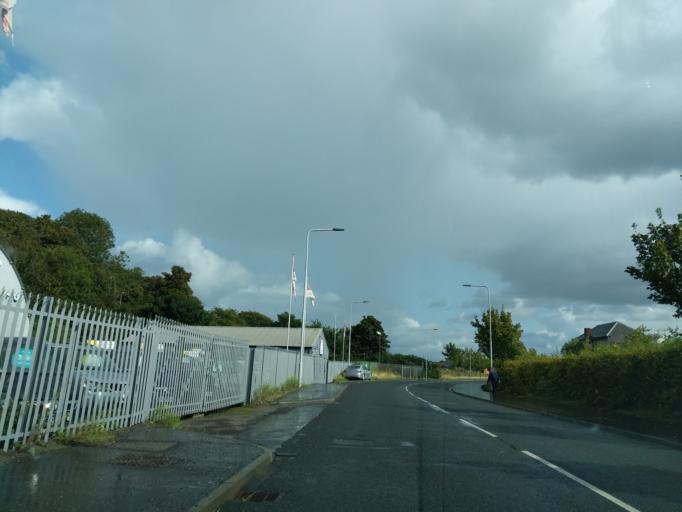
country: GB
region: Scotland
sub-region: Fife
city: Rosyth
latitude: 56.0245
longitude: -3.4311
